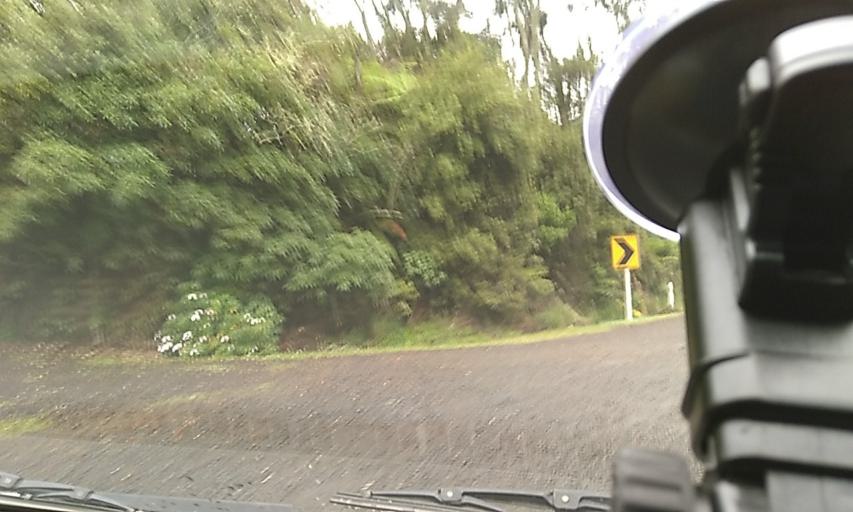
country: NZ
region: Auckland
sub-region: Auckland
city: Pukekohe East
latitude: -37.2997
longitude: 174.9362
